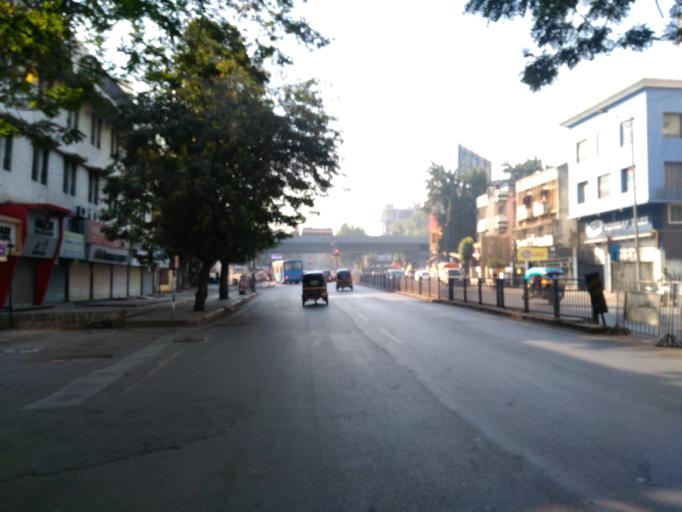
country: IN
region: Maharashtra
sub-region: Pune Division
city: Pune
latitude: 18.5025
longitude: 73.8691
